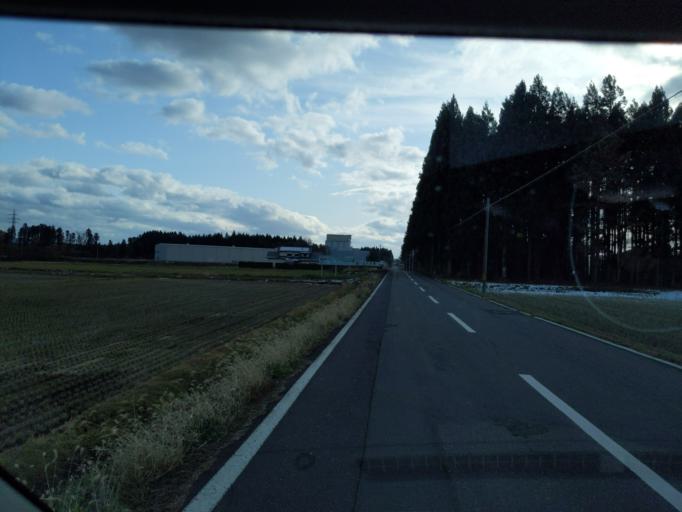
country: JP
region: Iwate
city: Mizusawa
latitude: 39.1091
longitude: 141.0821
